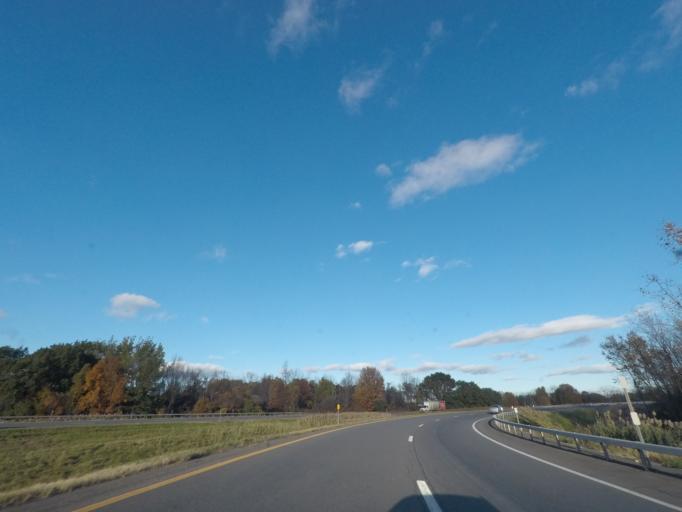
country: US
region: New York
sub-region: Albany County
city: Cohoes
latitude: 42.7637
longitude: -73.7655
